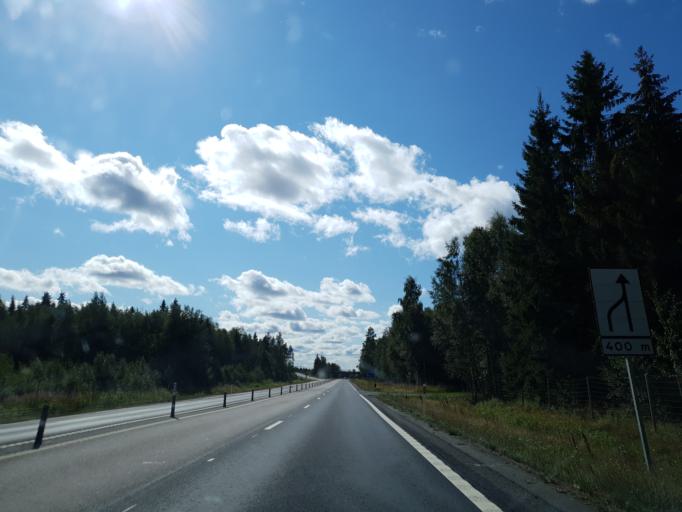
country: SE
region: Vaesterbotten
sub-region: Nordmalings Kommun
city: Nordmaling
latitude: 63.5416
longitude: 19.4066
